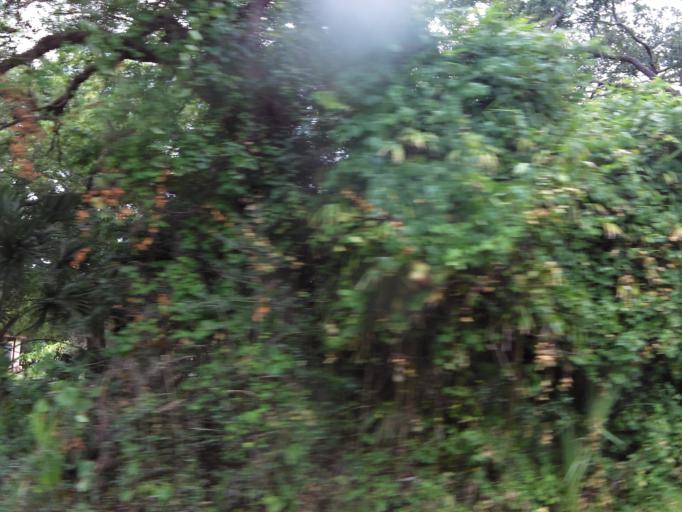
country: US
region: Florida
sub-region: Duval County
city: Atlantic Beach
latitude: 30.3400
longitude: -81.4219
